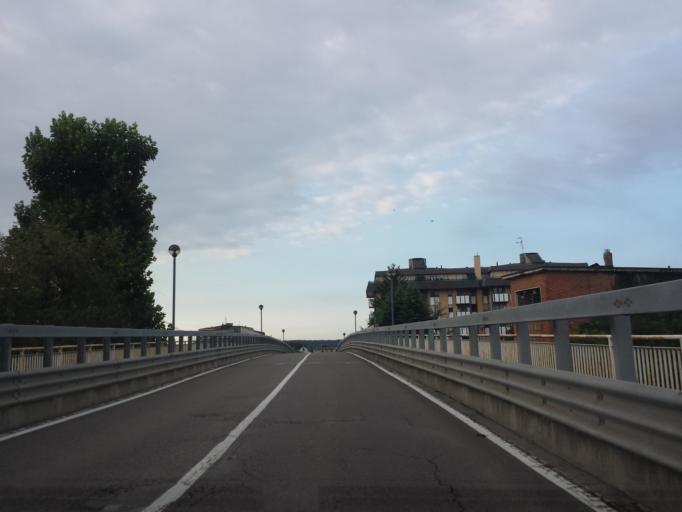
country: IT
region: Lombardy
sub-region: Provincia di Varese
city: Sesto Calende
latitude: 45.7289
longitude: 8.6323
